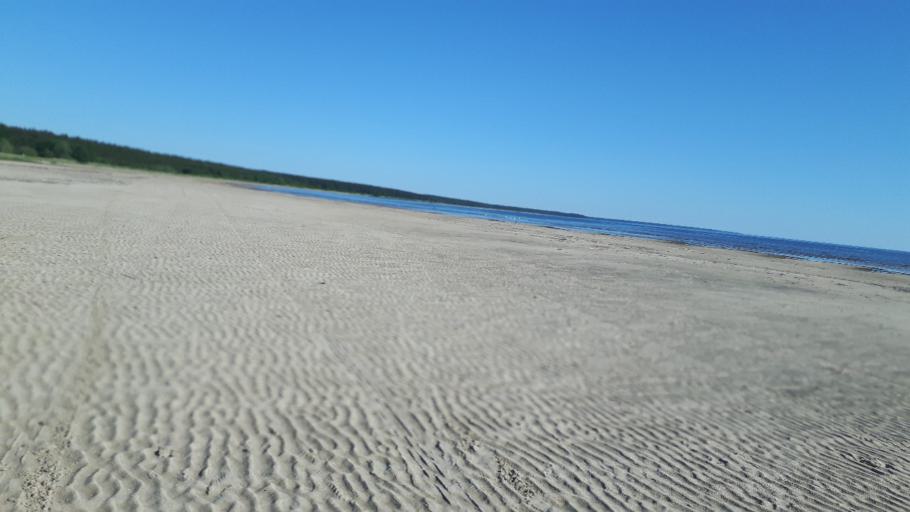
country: LV
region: Salacgrivas
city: Salacgriva
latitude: 57.6969
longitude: 24.3450
